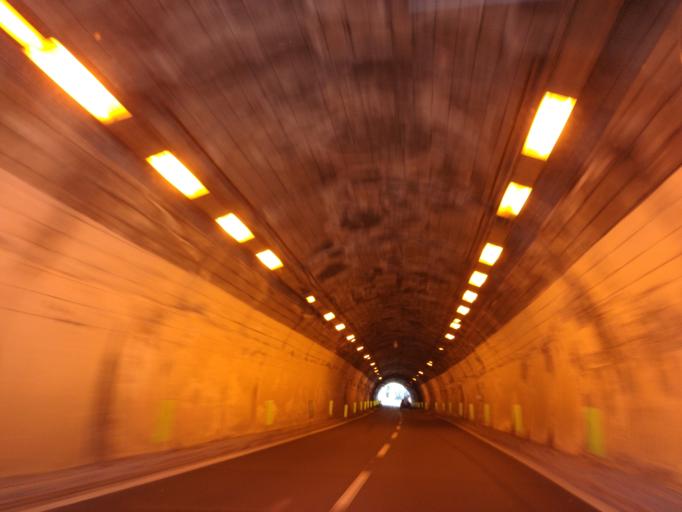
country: IT
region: Sicily
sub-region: Messina
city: Taormina
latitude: 37.8617
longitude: 15.2945
